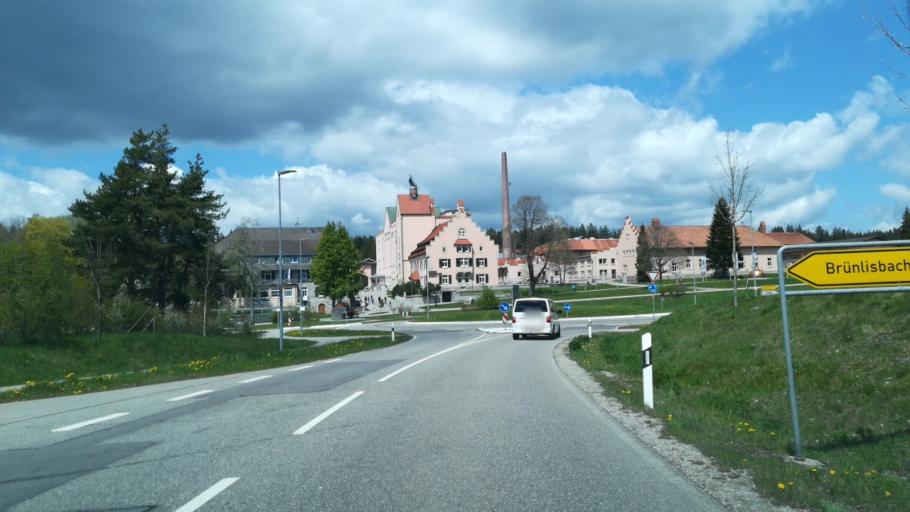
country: DE
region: Baden-Wuerttemberg
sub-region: Freiburg Region
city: Grafenhausen
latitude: 47.7940
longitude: 8.2454
